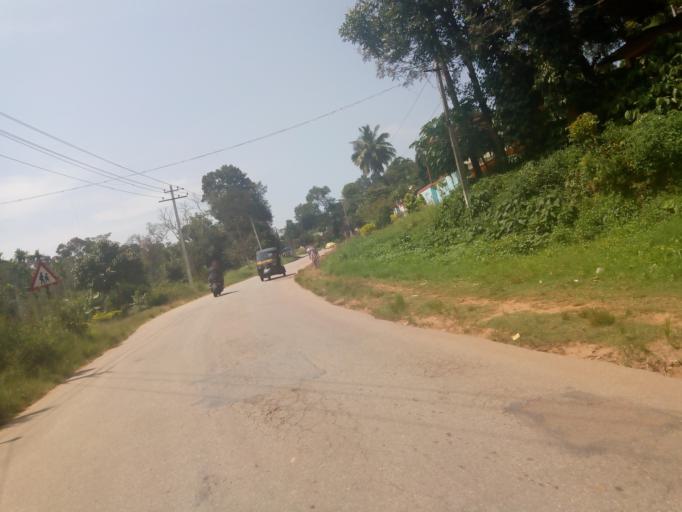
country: IN
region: Karnataka
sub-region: Kodagu
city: Ponnampet
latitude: 12.1227
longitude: 75.9403
